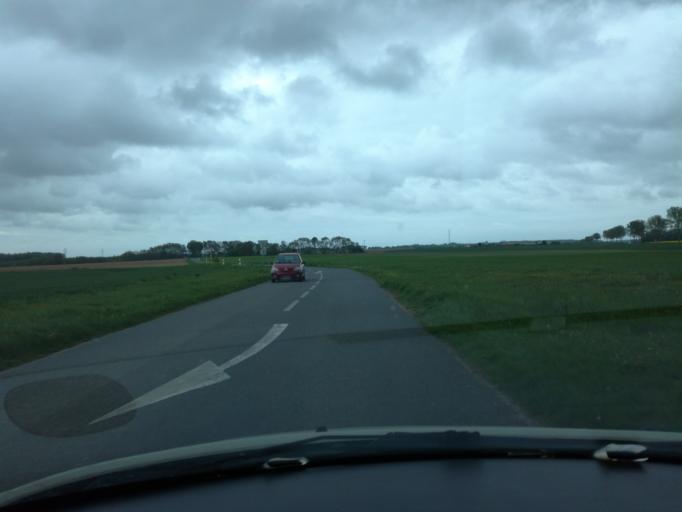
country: FR
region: Picardie
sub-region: Departement de la Somme
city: Poix-de-Picardie
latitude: 49.8214
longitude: 1.9570
